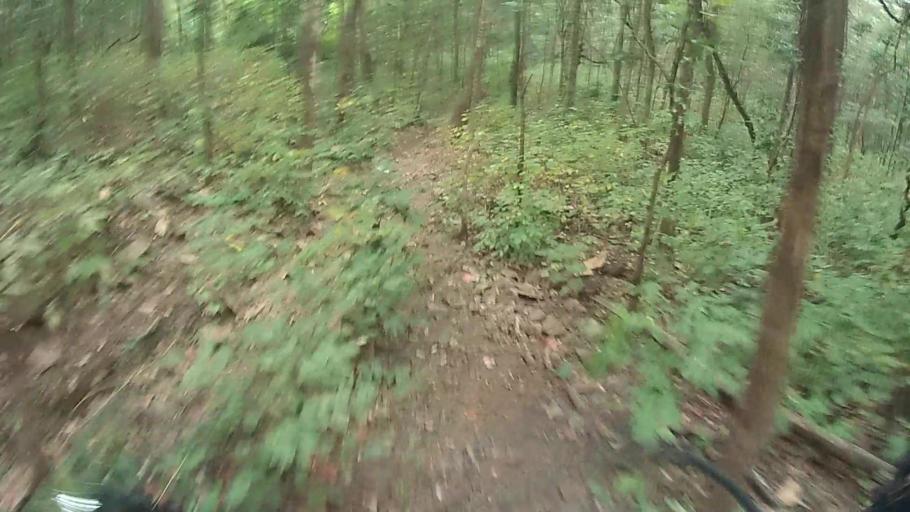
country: TH
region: Chiang Mai
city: Mae On
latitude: 18.7354
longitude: 99.2524
